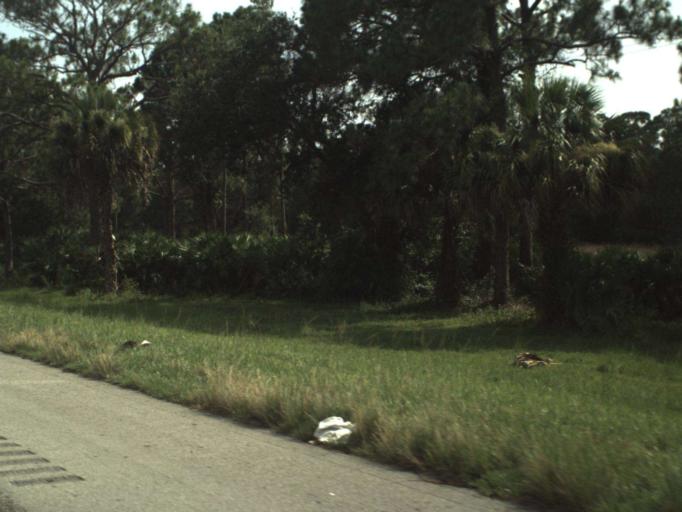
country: US
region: Florida
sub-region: Saint Lucie County
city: River Park
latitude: 27.3480
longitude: -80.4144
